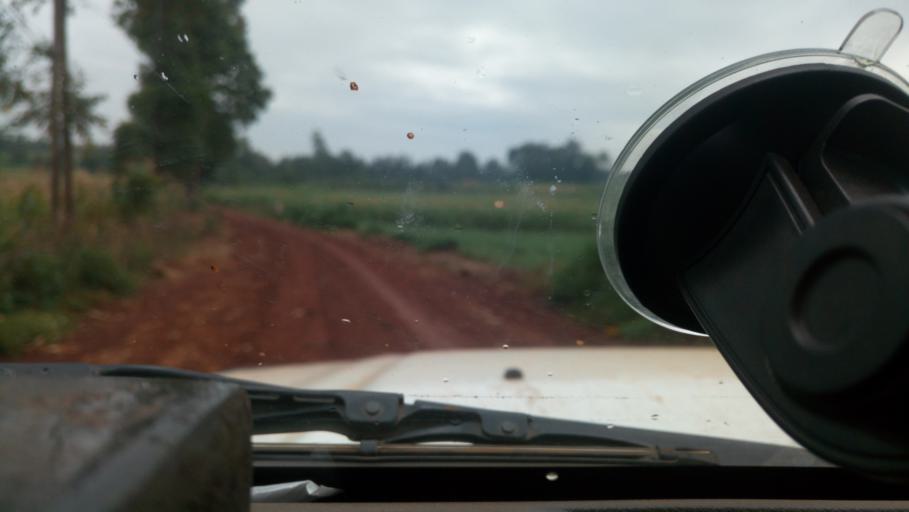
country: KE
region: Kisii
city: Ogembo
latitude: -0.9214
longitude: 34.6251
